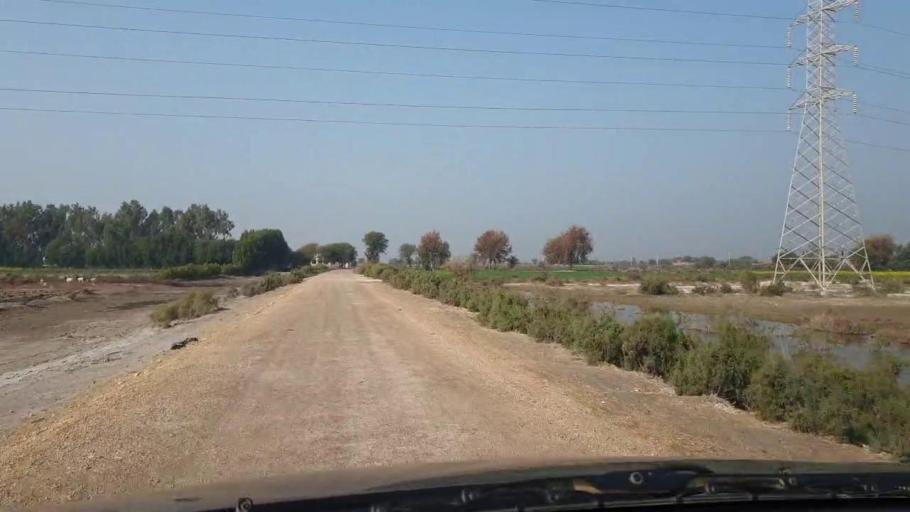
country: PK
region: Sindh
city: Sanghar
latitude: 25.9827
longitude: 68.9665
